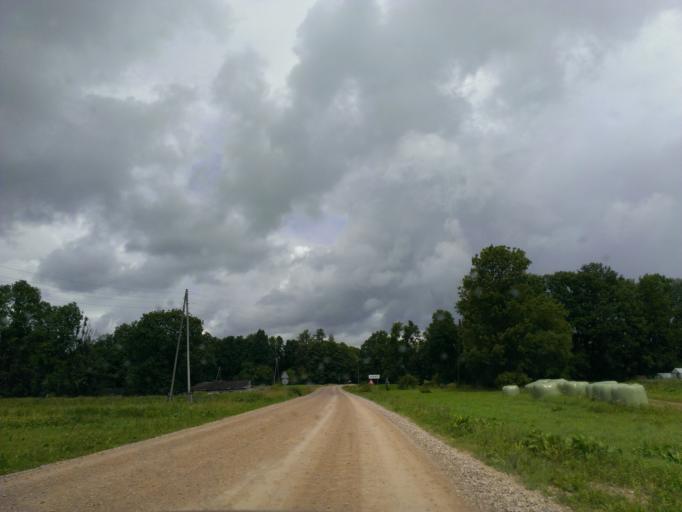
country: LV
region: Sigulda
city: Sigulda
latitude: 57.1976
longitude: 24.9467
